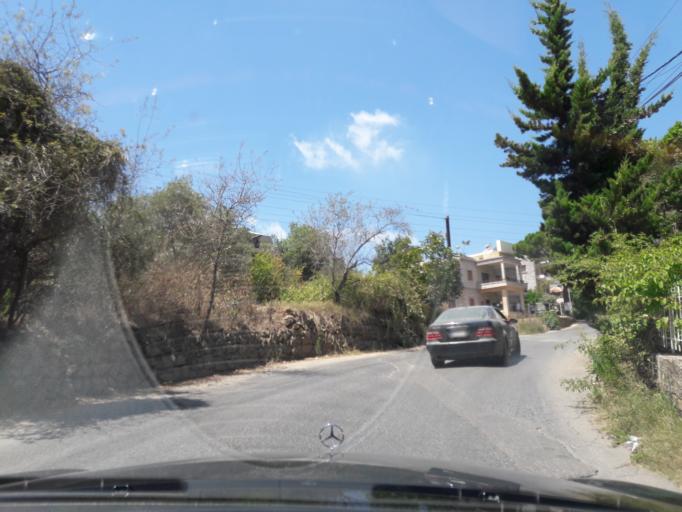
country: LB
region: Mont-Liban
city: Djounie
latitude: 33.9250
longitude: 35.6567
